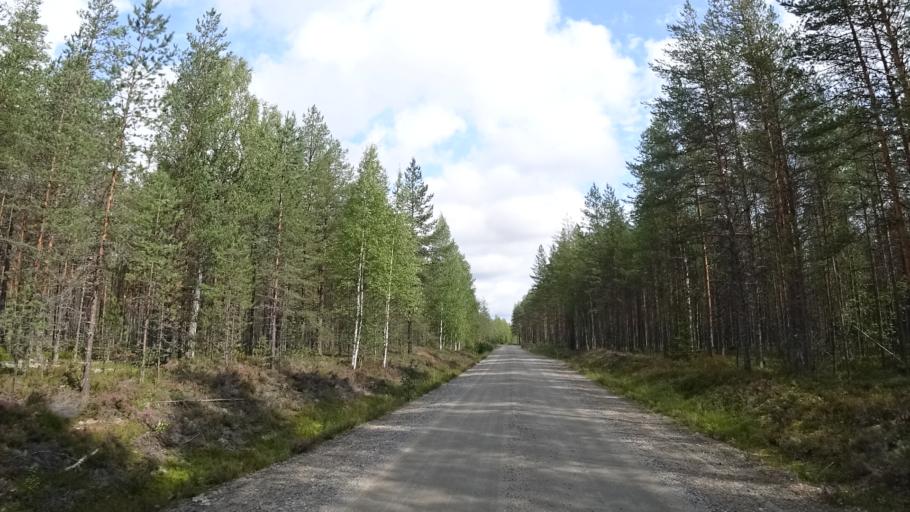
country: FI
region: North Karelia
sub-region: Joensuu
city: Ilomantsi
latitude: 62.9307
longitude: 31.4162
